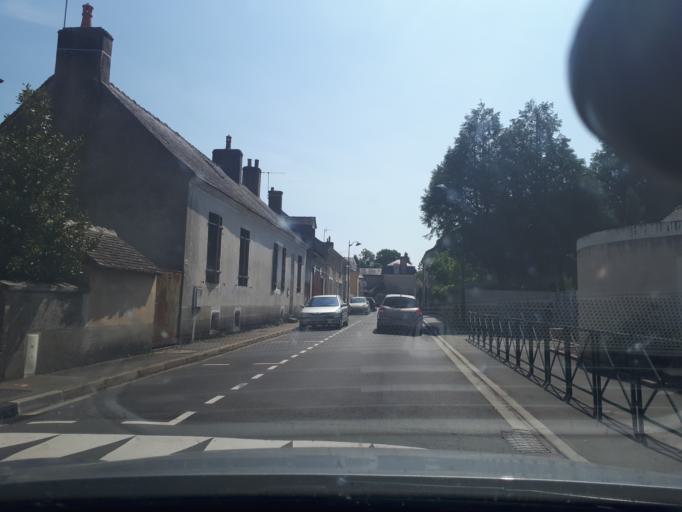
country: FR
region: Pays de la Loire
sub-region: Departement de la Sarthe
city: Le Breil-sur-Merize
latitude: 48.0091
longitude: 0.4764
